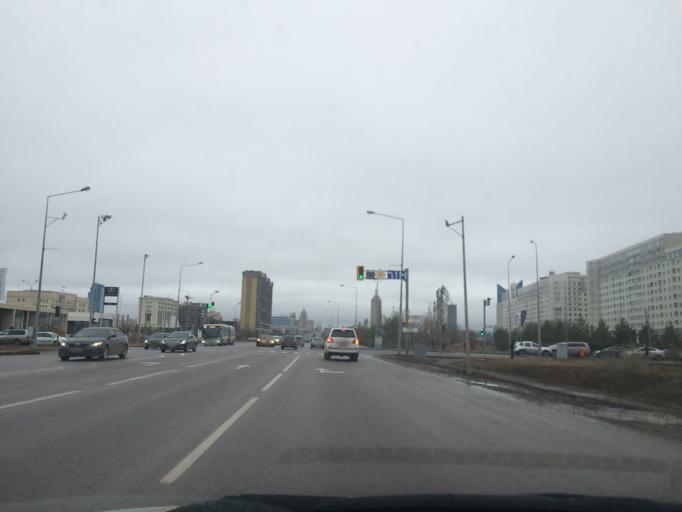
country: KZ
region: Astana Qalasy
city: Astana
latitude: 51.1177
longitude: 71.4118
